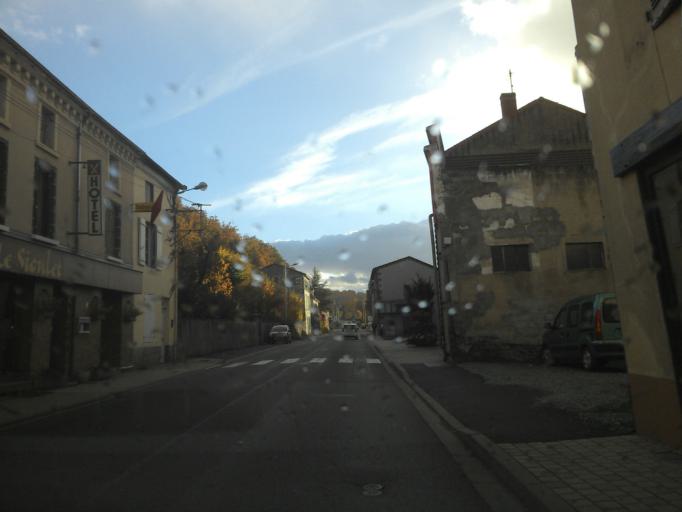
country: FR
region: Auvergne
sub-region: Departement du Puy-de-Dome
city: Gelles
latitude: 45.8679
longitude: 2.6757
